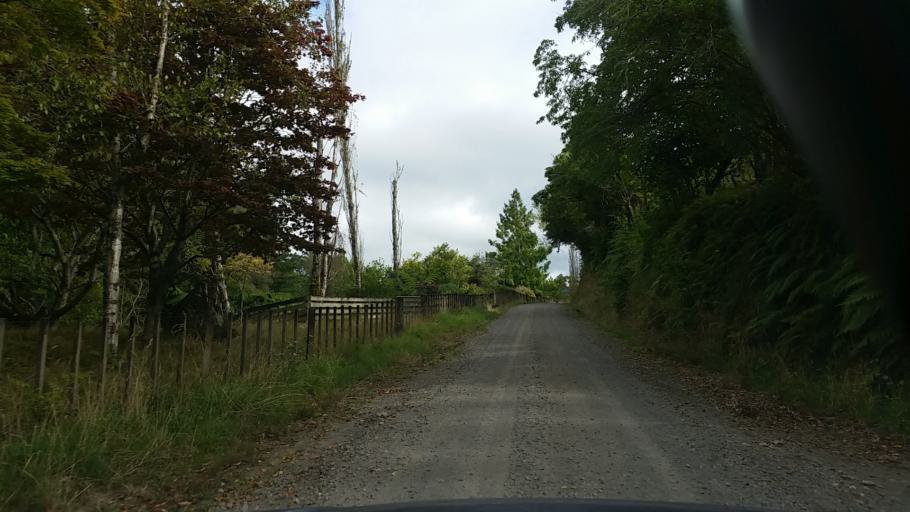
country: NZ
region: Taranaki
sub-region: South Taranaki District
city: Eltham
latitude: -39.3589
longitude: 174.5125
